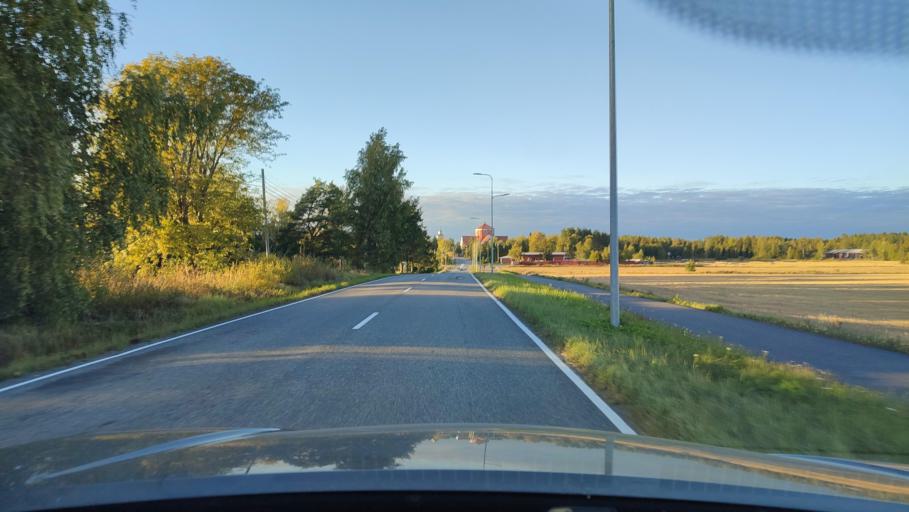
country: FI
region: Ostrobothnia
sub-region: Sydosterbotten
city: Kristinestad
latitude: 62.2405
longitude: 21.5209
